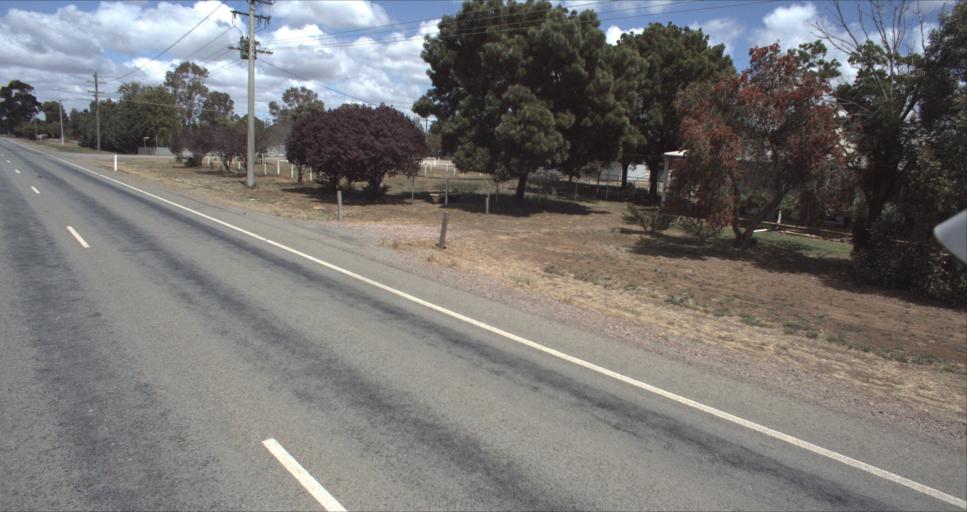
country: AU
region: New South Wales
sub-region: Murrumbidgee Shire
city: Darlington Point
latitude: -34.5116
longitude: 146.1862
